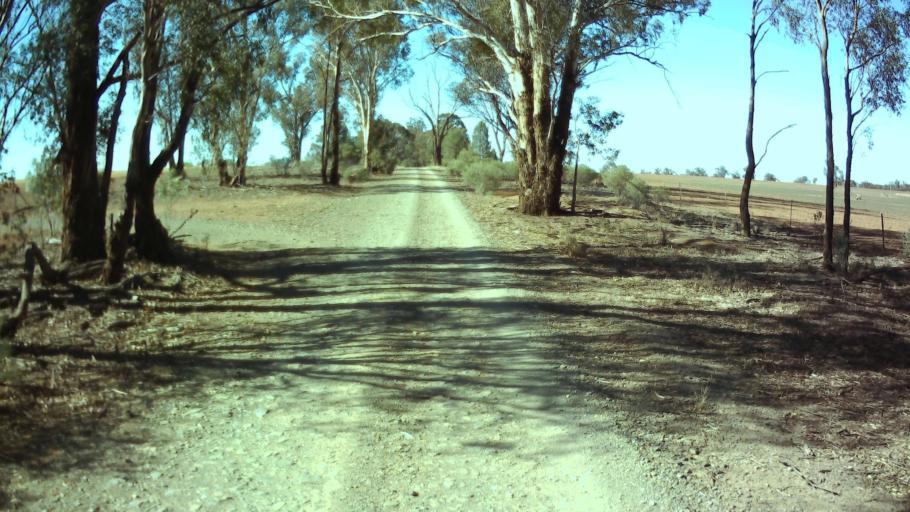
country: AU
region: New South Wales
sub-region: Weddin
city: Grenfell
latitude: -33.7432
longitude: 147.8315
